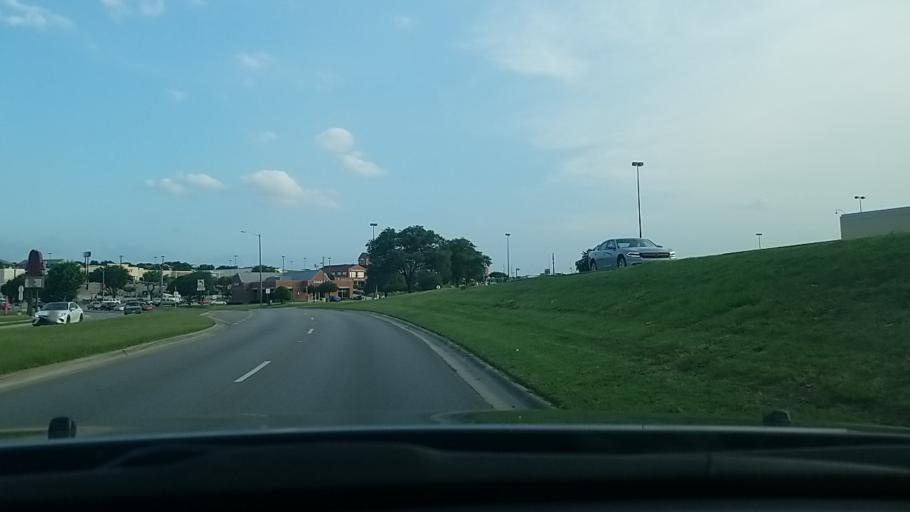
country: US
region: Texas
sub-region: Denton County
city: Denton
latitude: 33.1910
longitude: -97.1046
